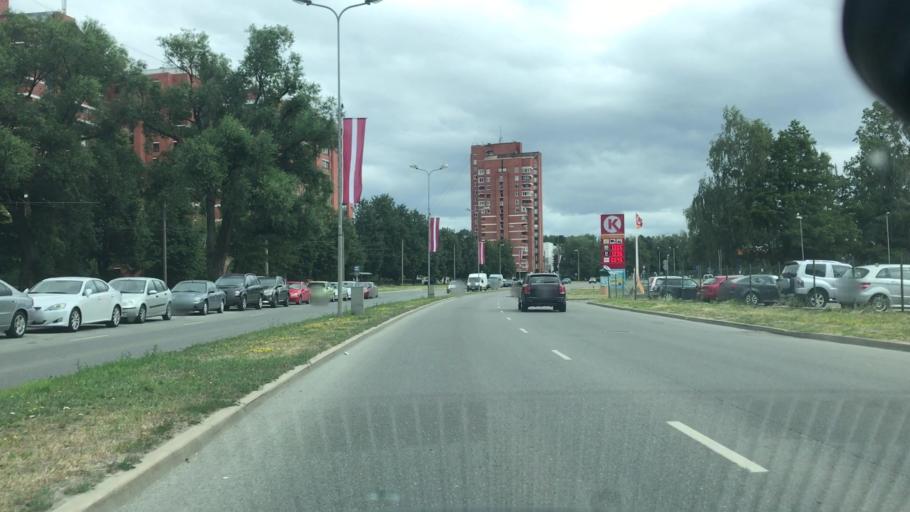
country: LV
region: Marupe
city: Marupe
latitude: 56.9602
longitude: 24.0164
